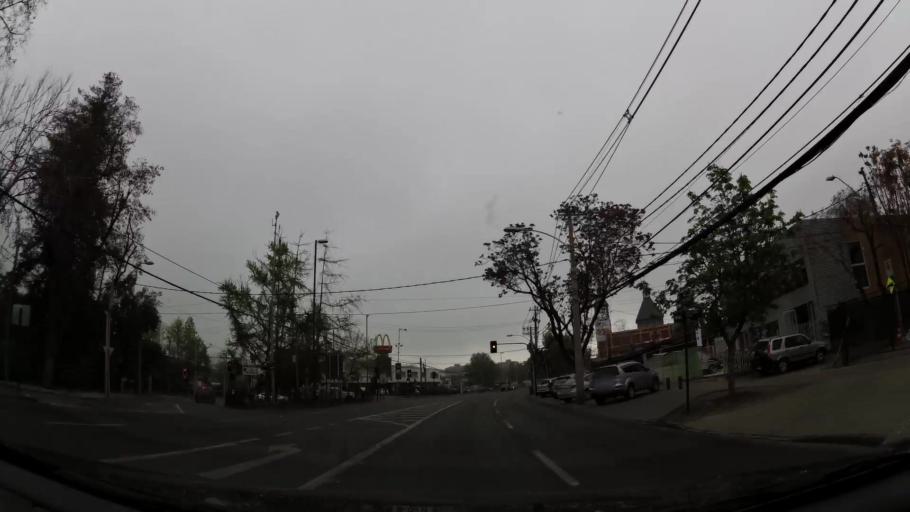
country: CL
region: Santiago Metropolitan
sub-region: Provincia de Santiago
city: Villa Presidente Frei, Nunoa, Santiago, Chile
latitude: -33.3864
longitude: -70.5640
